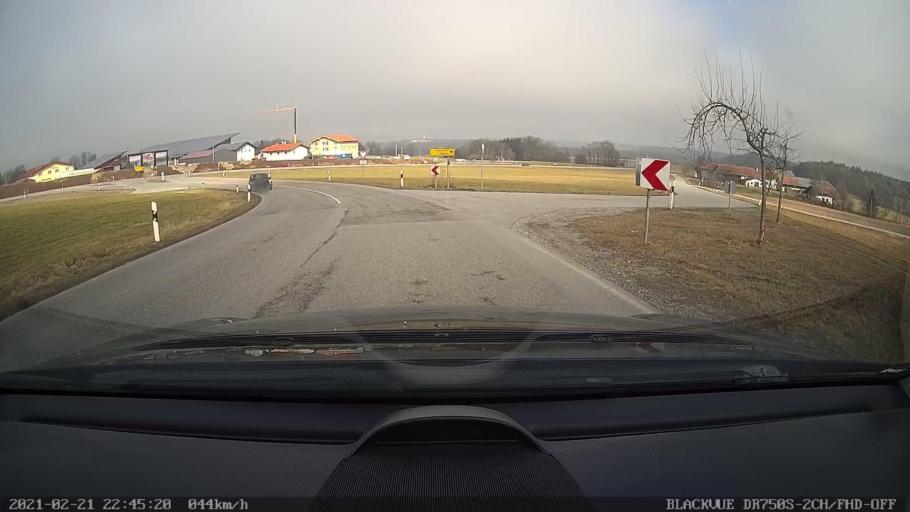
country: DE
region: Bavaria
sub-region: Upper Bavaria
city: Griesstatt
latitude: 48.0003
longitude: 12.1795
